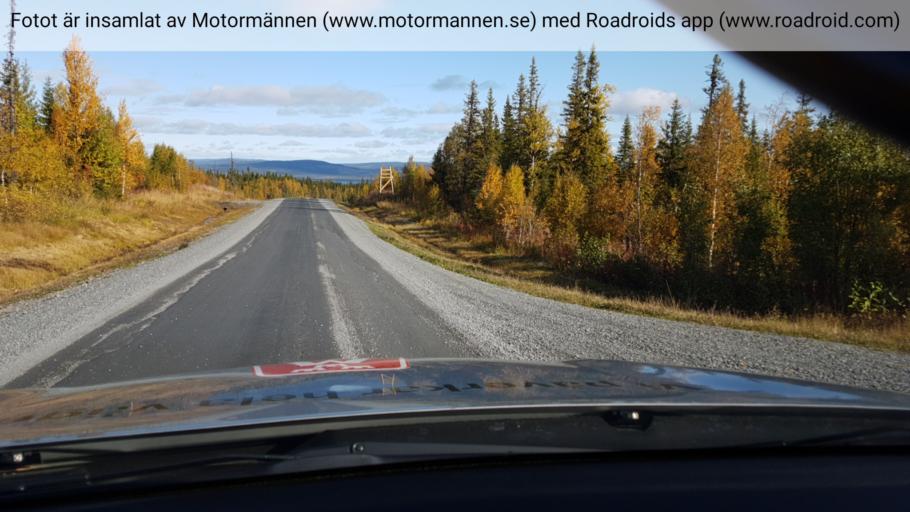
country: SE
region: Vaesterbotten
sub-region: Vilhelmina Kommun
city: Sjoberg
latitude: 64.7754
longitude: 15.9470
